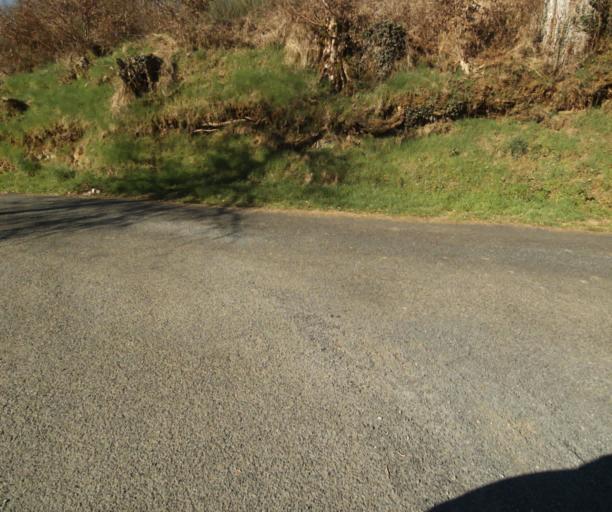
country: FR
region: Limousin
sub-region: Departement de la Correze
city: Seilhac
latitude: 45.3821
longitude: 1.7706
